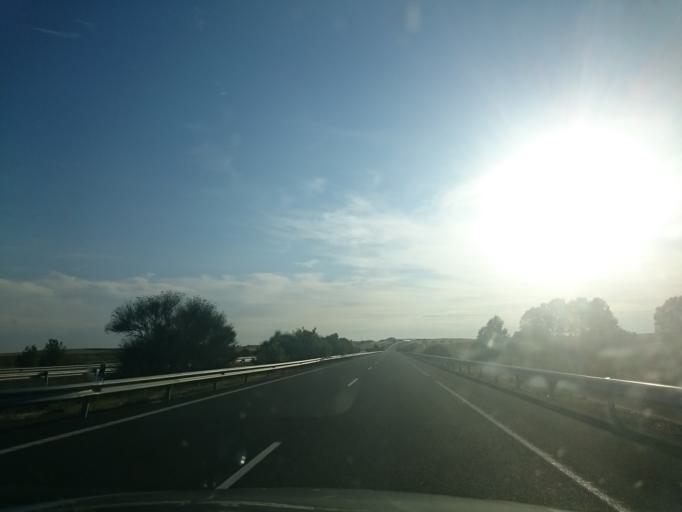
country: ES
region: Castille and Leon
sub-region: Provincia de Palencia
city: Moratinos
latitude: 42.3641
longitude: -4.9069
